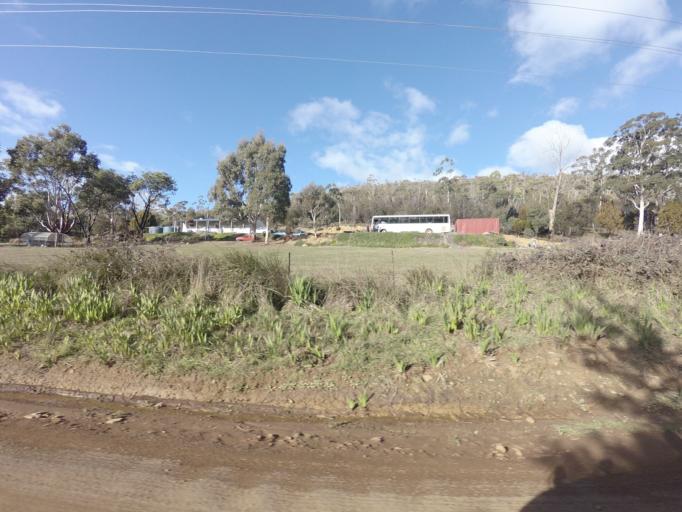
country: AU
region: Tasmania
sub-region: Derwent Valley
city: New Norfolk
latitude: -42.8093
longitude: 147.1329
